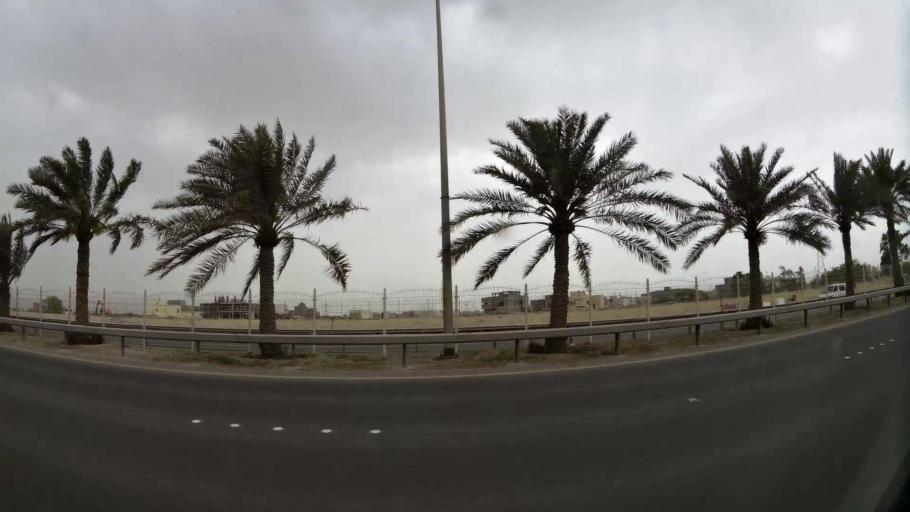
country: BH
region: Northern
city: Madinat `Isa
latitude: 26.1623
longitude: 50.5410
